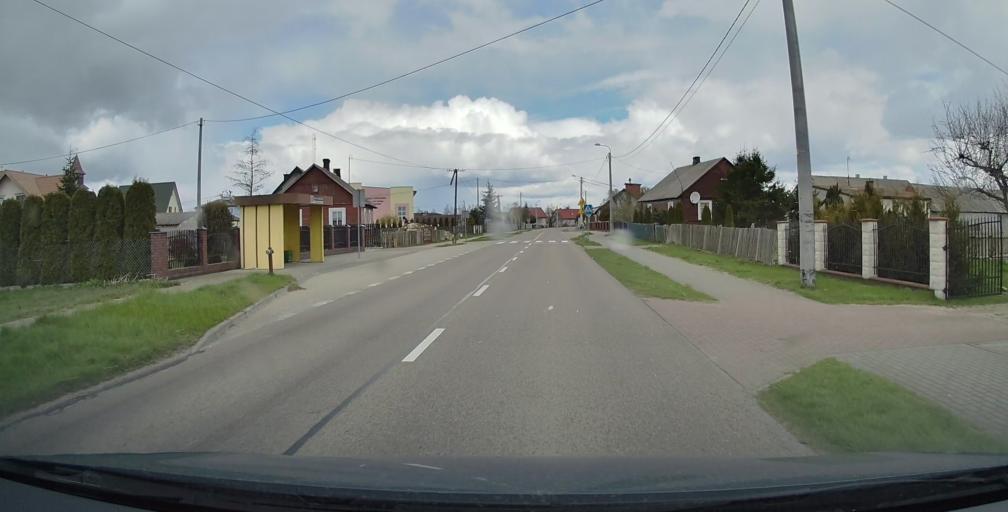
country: PL
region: Masovian Voivodeship
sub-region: Powiat ostrolecki
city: Rzekun
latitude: 52.9948
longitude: 21.5897
